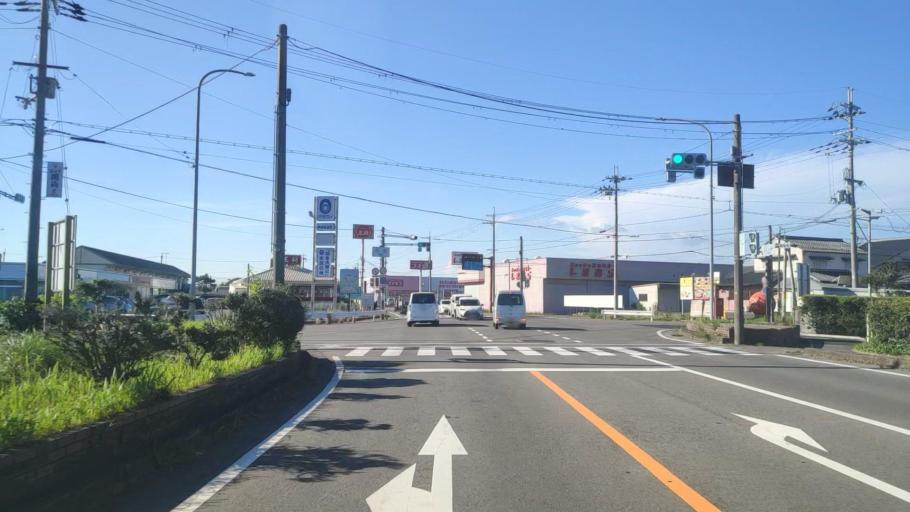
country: JP
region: Shiga Prefecture
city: Hino
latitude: 35.0112
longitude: 136.2402
